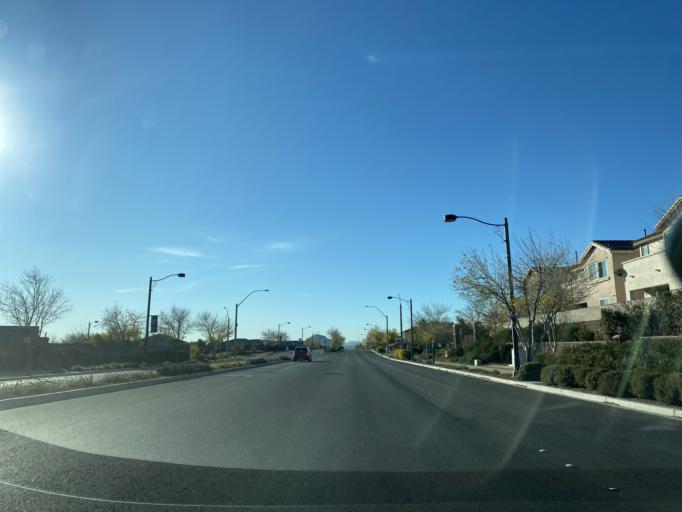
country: US
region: Nevada
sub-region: Clark County
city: Summerlin South
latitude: 36.2930
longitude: -115.3196
